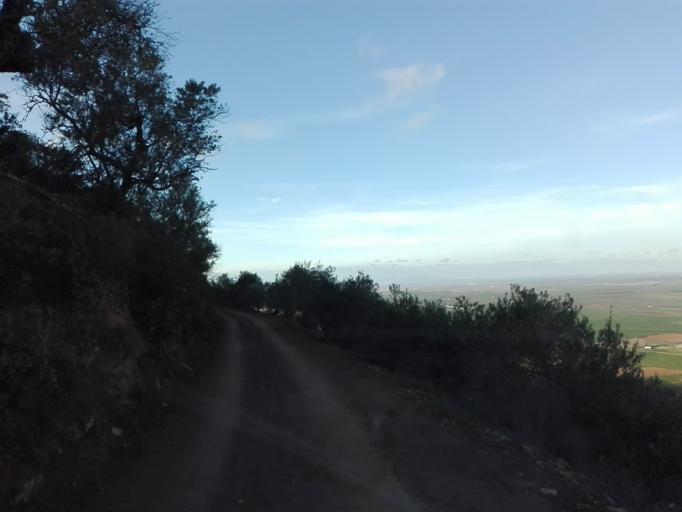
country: ES
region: Extremadura
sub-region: Provincia de Badajoz
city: Llerena
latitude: 38.2135
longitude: -5.9965
